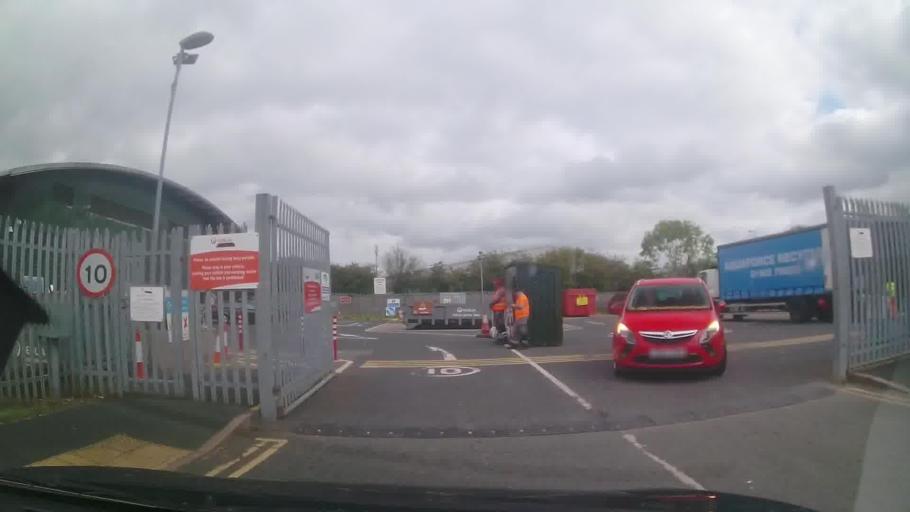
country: GB
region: England
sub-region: Shropshire
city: Whitchurch
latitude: 52.9646
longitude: -2.6698
